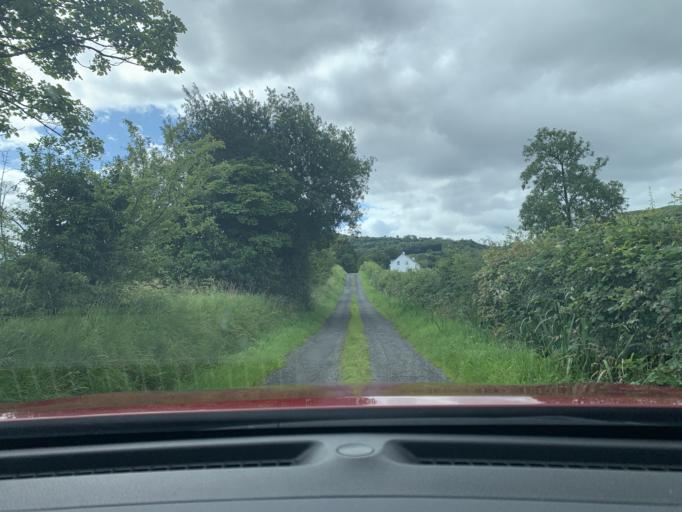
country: GB
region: Northern Ireland
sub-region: Fermanagh District
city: Enniskillen
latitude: 54.2747
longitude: -7.8074
